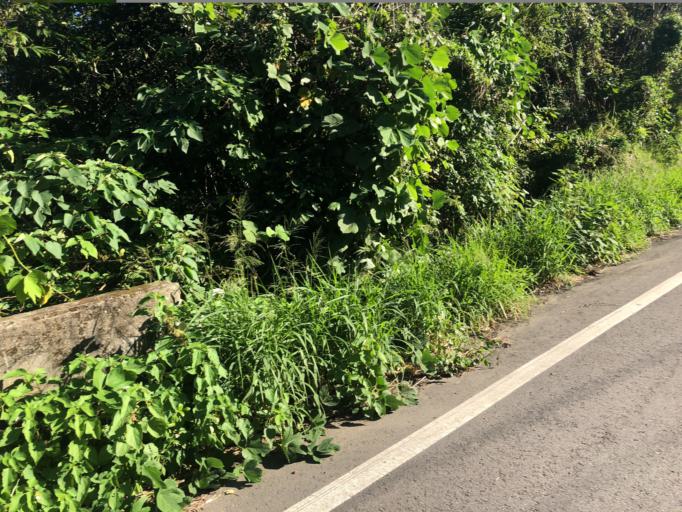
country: TW
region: Taiwan
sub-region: Hsinchu
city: Hsinchu
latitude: 24.7506
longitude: 120.9763
